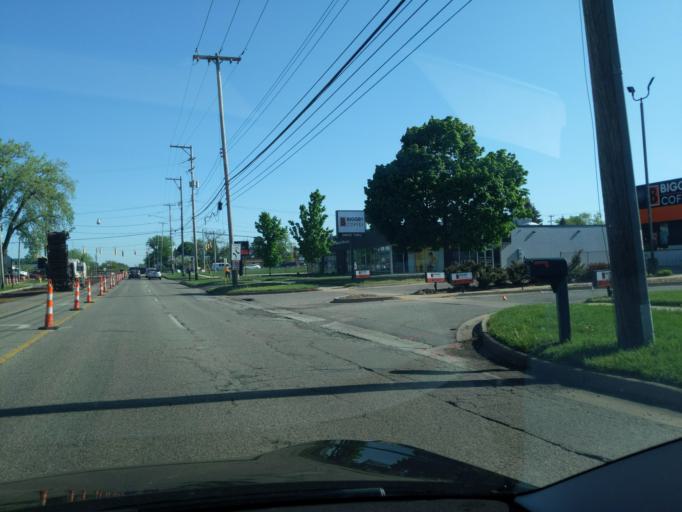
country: US
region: Michigan
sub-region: Kent County
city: East Grand Rapids
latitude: 42.9113
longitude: -85.5685
